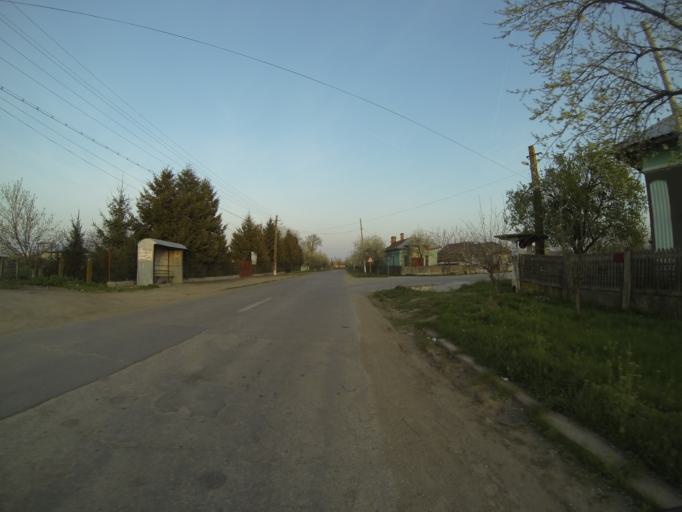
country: RO
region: Dolj
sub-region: Comuna Dranicu
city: Dranic
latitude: 44.0568
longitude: 23.8355
